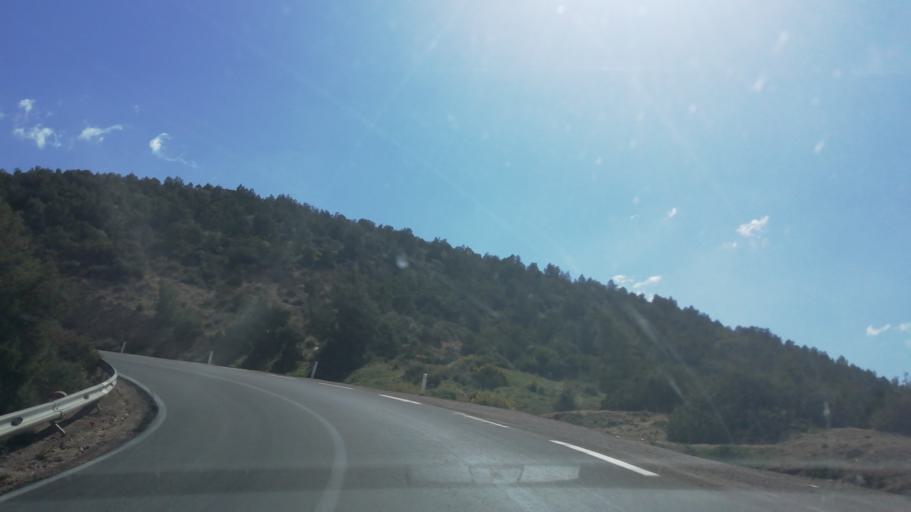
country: DZ
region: Mascara
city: Mascara
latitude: 35.4874
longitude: 0.1504
